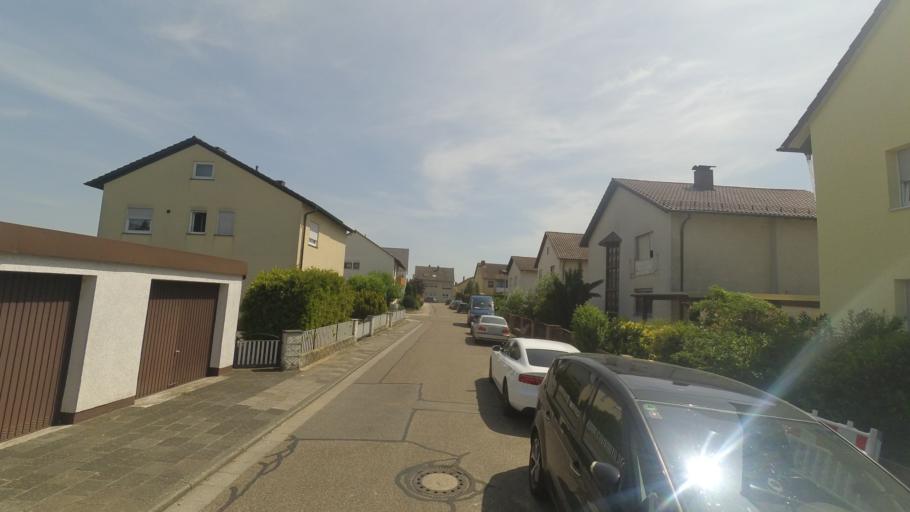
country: DE
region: Rheinland-Pfalz
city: Waldsee
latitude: 49.3929
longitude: 8.4331
